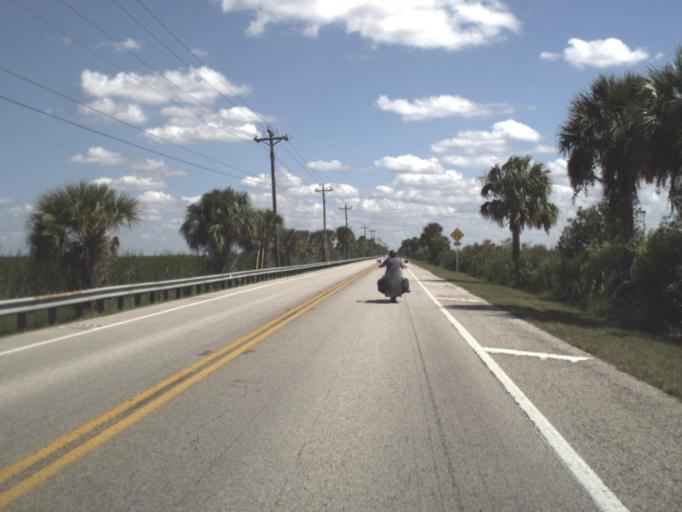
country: US
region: Florida
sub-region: Collier County
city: Marco
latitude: 25.9288
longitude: -81.4341
